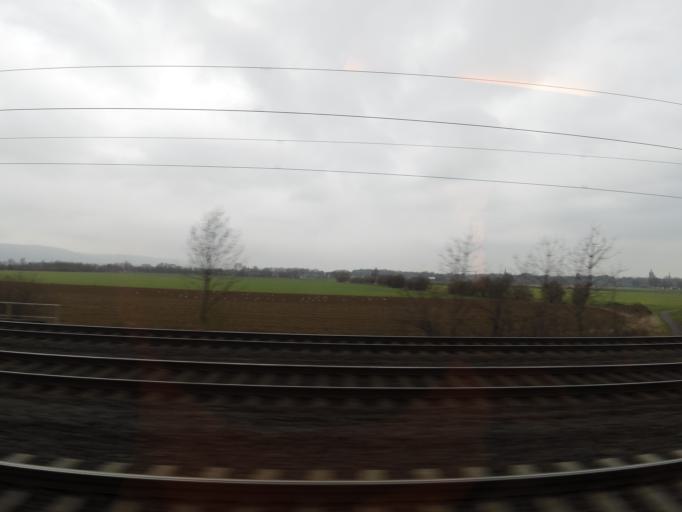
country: DE
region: North Rhine-Westphalia
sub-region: Regierungsbezirk Detmold
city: Minden
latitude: 52.2787
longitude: 8.9330
